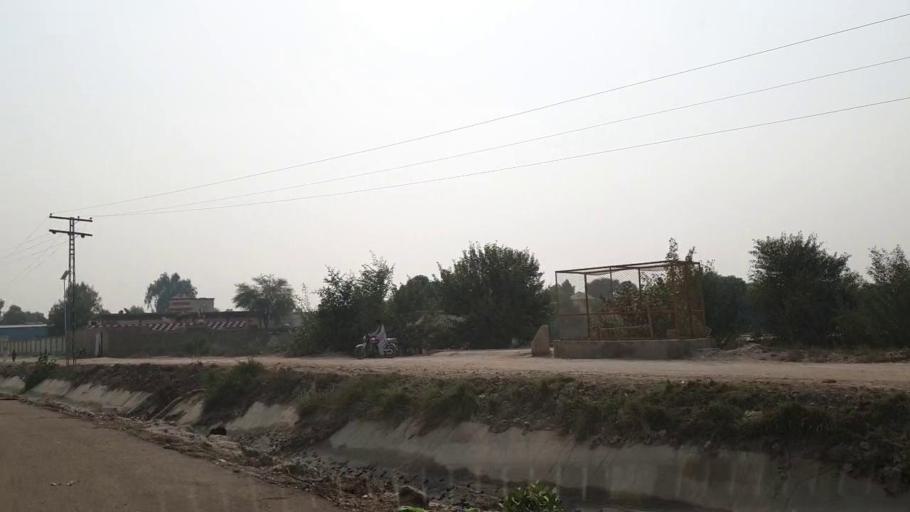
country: PK
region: Sindh
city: Bhan
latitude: 26.5196
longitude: 67.7148
